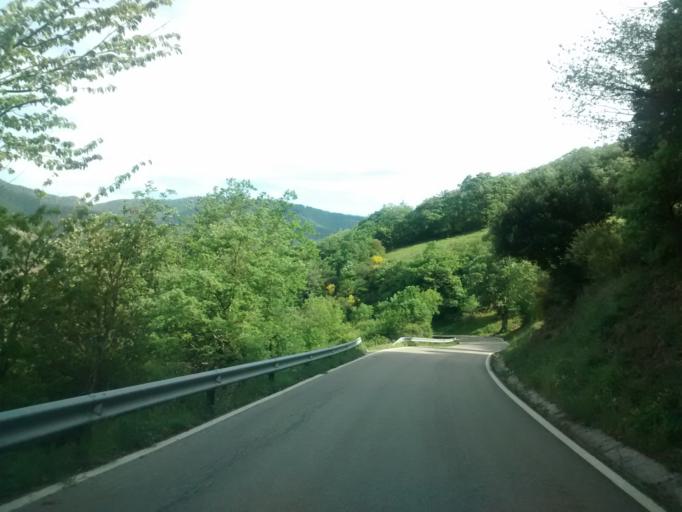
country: ES
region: Cantabria
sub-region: Provincia de Cantabria
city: Potes
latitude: 43.1893
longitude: -4.6123
